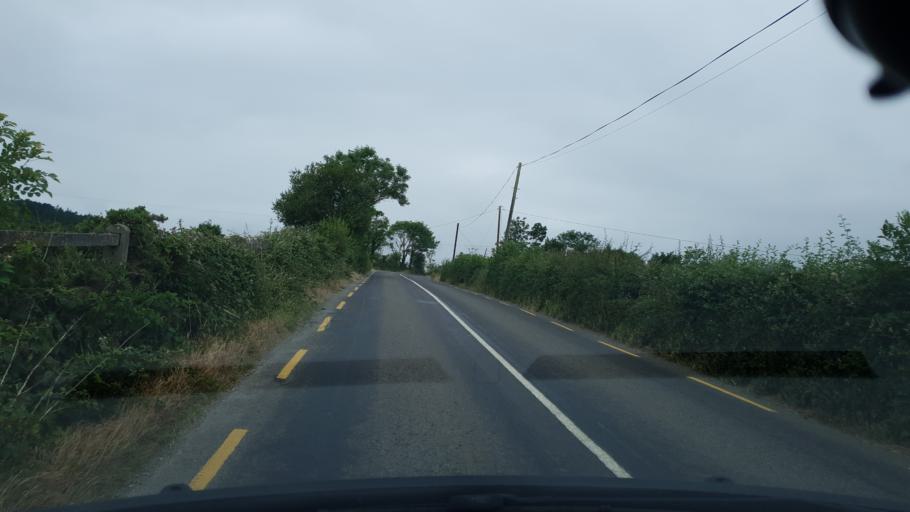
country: IE
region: Munster
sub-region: Ciarrai
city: Tralee
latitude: 52.1585
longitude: -9.6732
